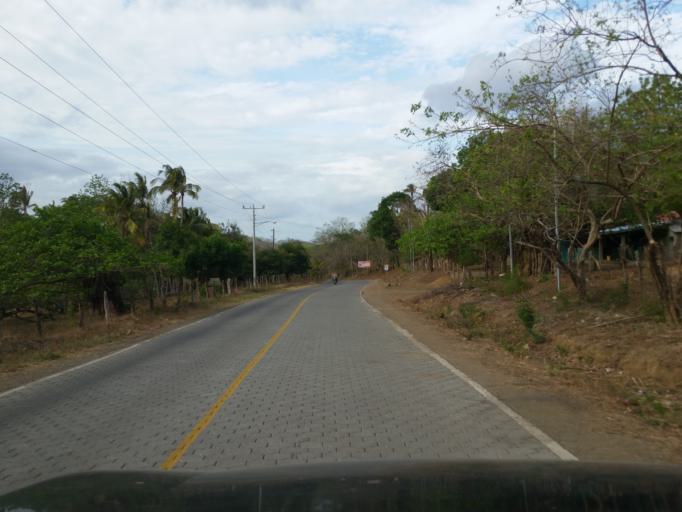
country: NI
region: Rivas
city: Tola
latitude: 11.4128
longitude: -85.9527
